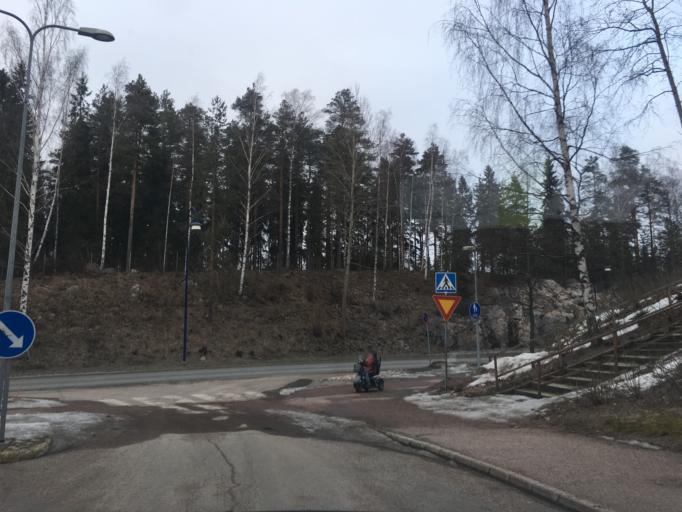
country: FI
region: Uusimaa
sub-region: Helsinki
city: Vantaa
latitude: 60.3243
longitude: 25.0713
